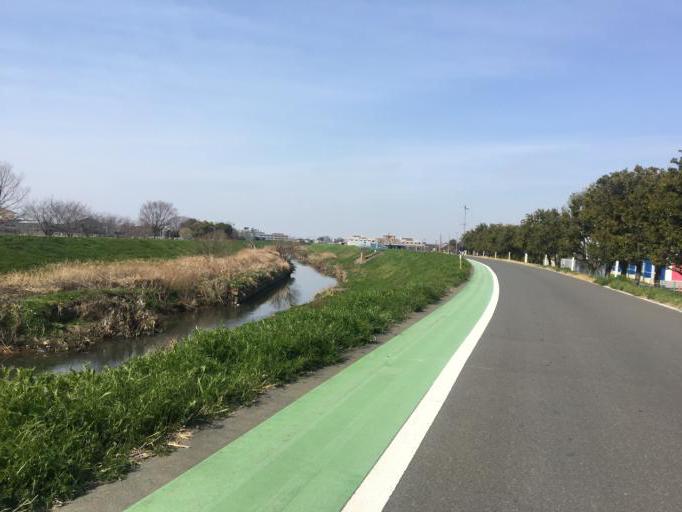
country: JP
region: Saitama
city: Kamifukuoka
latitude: 35.8710
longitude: 139.5493
